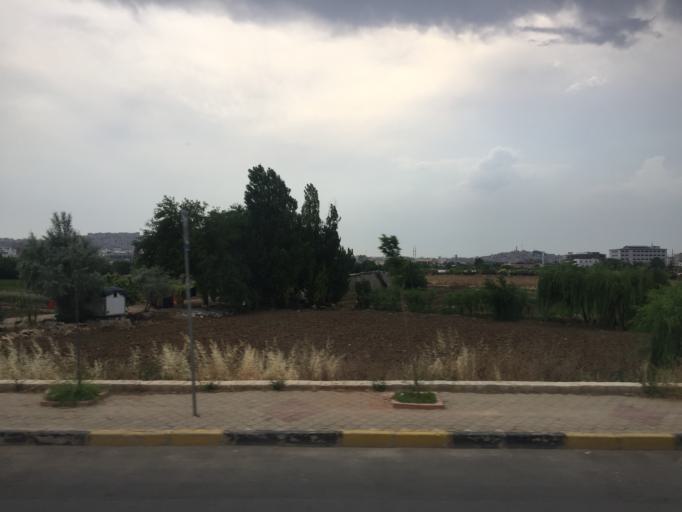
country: TR
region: Gaziantep
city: Gaziantep
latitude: 37.0585
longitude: 37.4157
